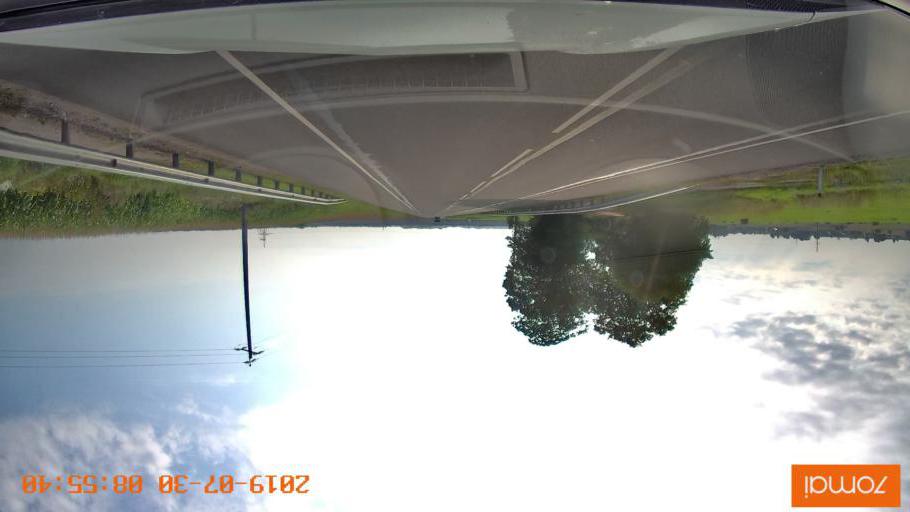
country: RU
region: Kaliningrad
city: Gusev
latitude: 54.6003
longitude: 22.0570
